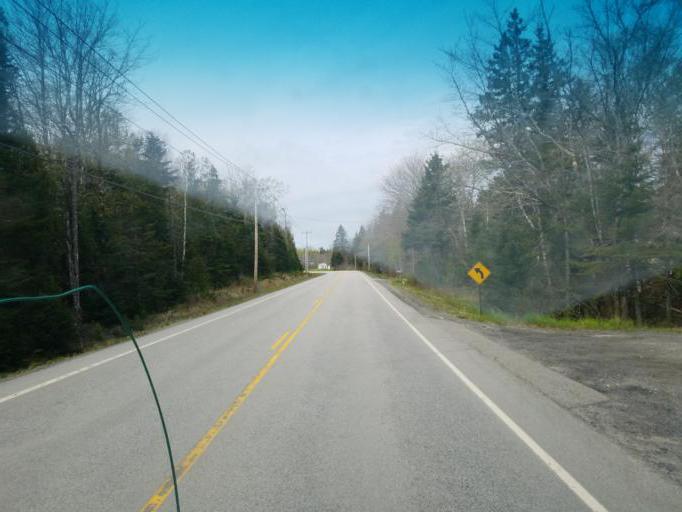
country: US
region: Maine
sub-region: Washington County
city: Eastport
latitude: 44.8014
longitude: -67.1337
